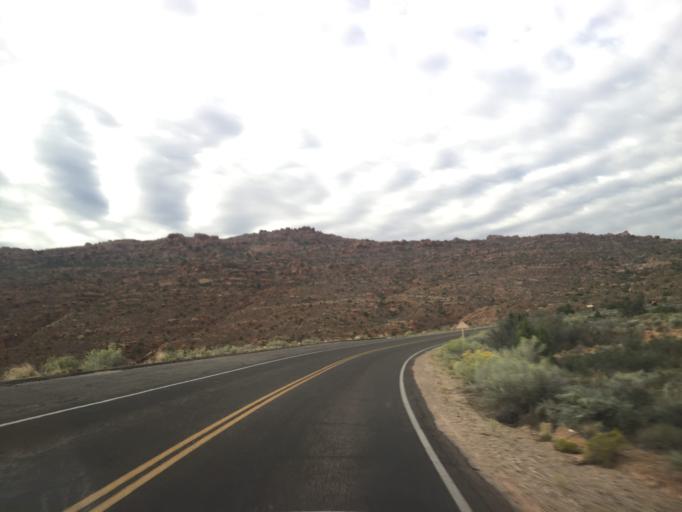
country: US
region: Utah
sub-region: Grand County
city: Moab
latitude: 38.7269
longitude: -109.5389
